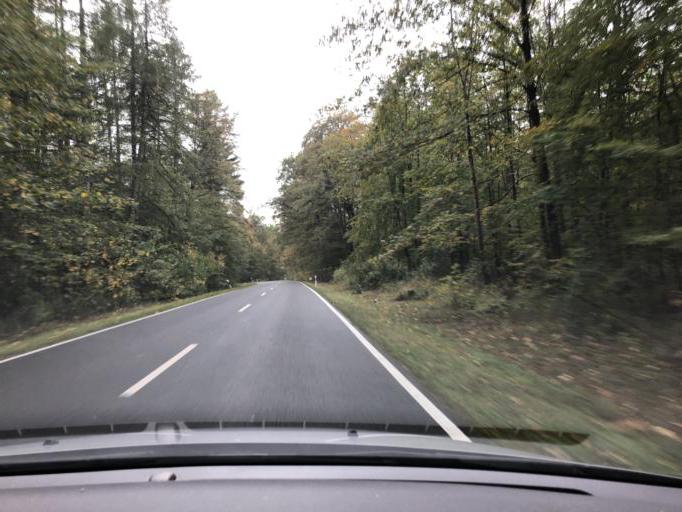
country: DE
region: Thuringia
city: Wachstedt
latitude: 51.2846
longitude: 10.2275
